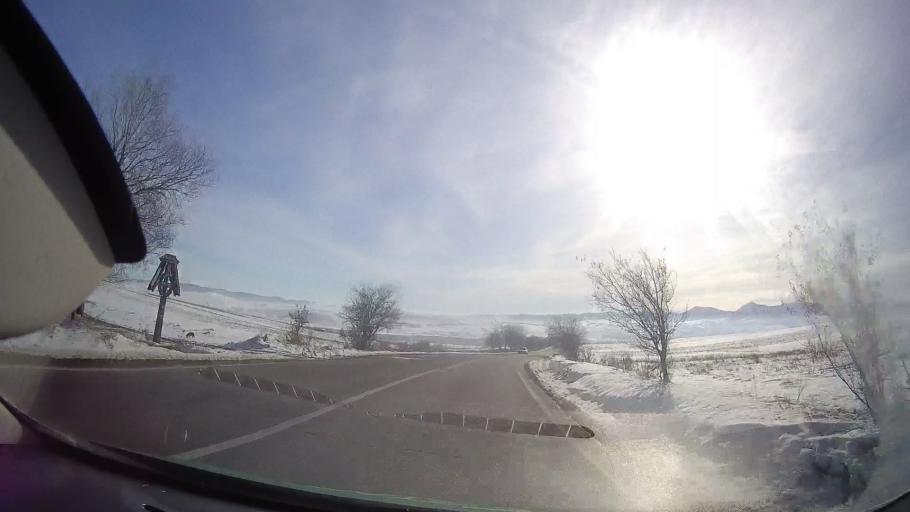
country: RO
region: Neamt
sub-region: Comuna Baltatesti
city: Valea Seaca
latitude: 47.1540
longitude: 26.3245
